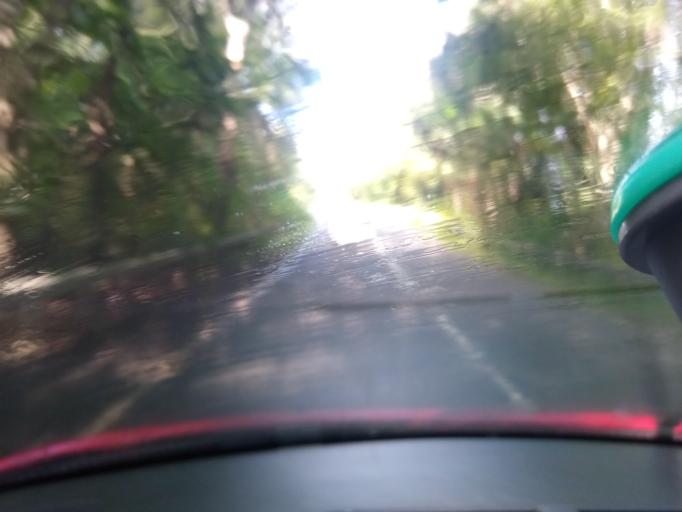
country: GB
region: Scotland
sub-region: The Scottish Borders
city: Jedburgh
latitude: 55.5712
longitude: -2.5369
